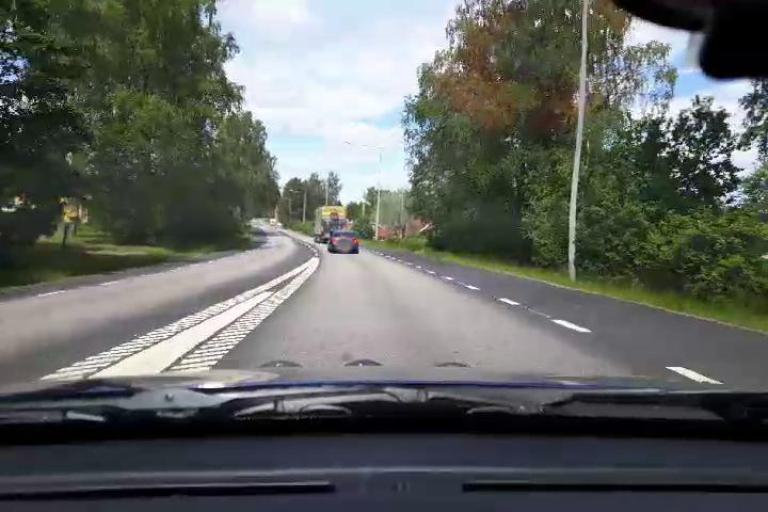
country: SE
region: Uppsala
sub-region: Osthammars Kommun
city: Bjorklinge
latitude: 60.0336
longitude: 17.5523
